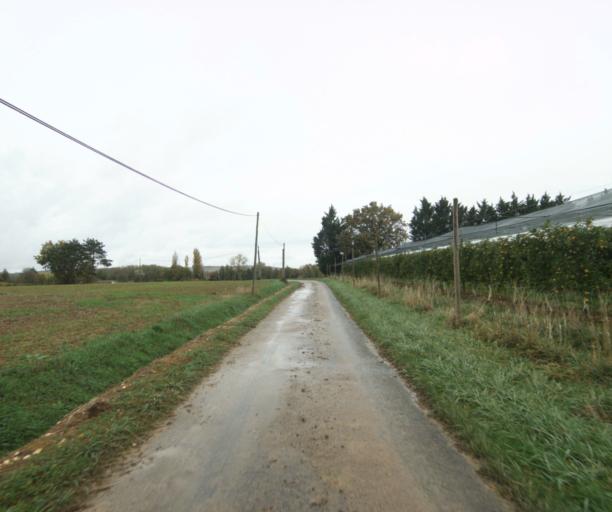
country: FR
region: Rhone-Alpes
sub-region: Departement de l'Ain
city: Pont-de-Vaux
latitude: 46.4786
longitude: 4.8805
